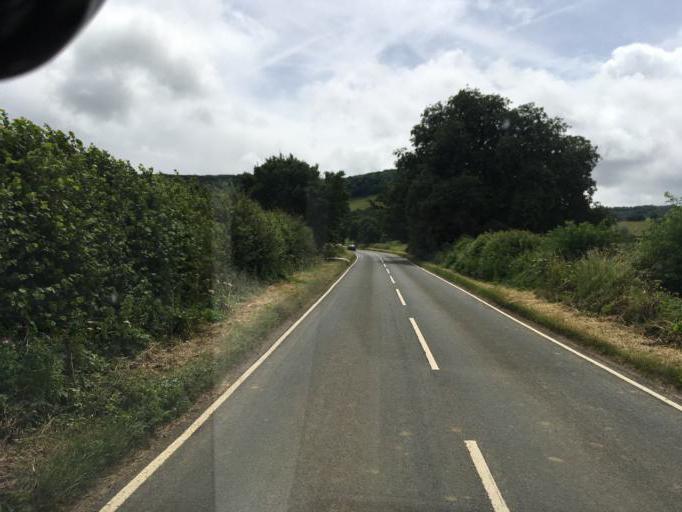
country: GB
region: England
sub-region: Gloucestershire
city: Stonehouse
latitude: 51.7226
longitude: -2.3081
